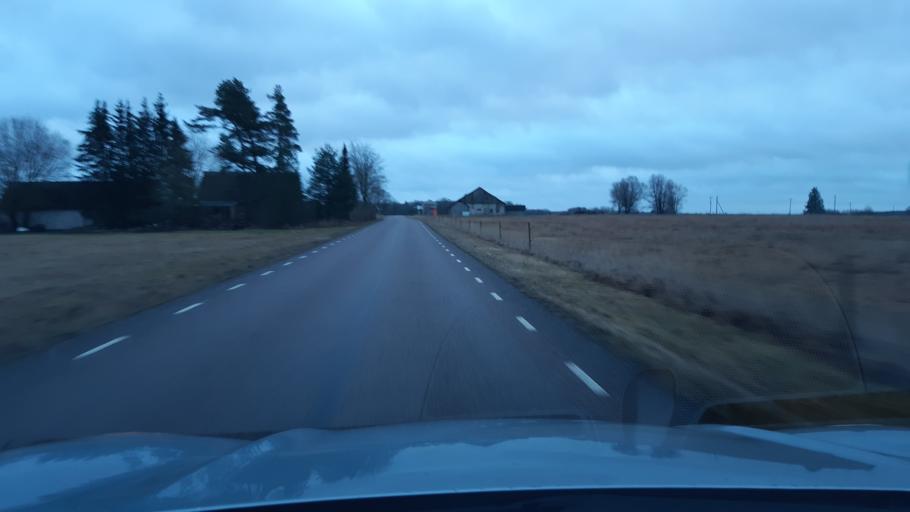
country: EE
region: Raplamaa
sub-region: Rapla vald
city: Rapla
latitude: 59.0171
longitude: 24.6979
